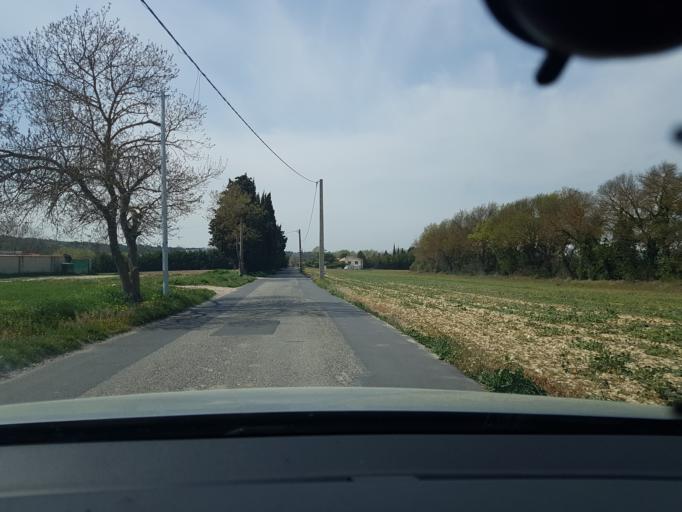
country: FR
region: Provence-Alpes-Cote d'Azur
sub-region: Departement des Bouches-du-Rhone
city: Cabries
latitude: 43.4768
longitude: 5.3852
